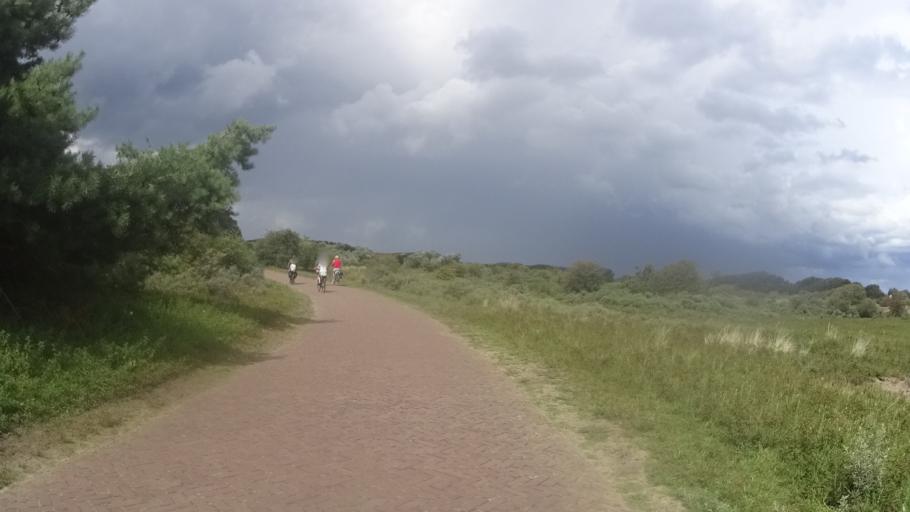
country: NL
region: North Holland
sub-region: Gemeente Bergen
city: Egmond aan Zee
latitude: 52.6043
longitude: 4.6416
